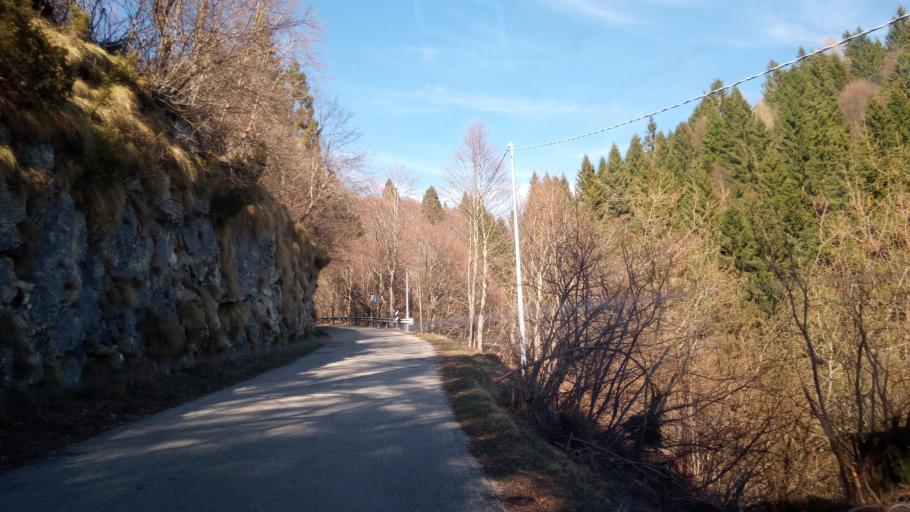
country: IT
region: Veneto
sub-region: Provincia di Treviso
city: Borso del Grappa
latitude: 45.8395
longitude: 11.7808
